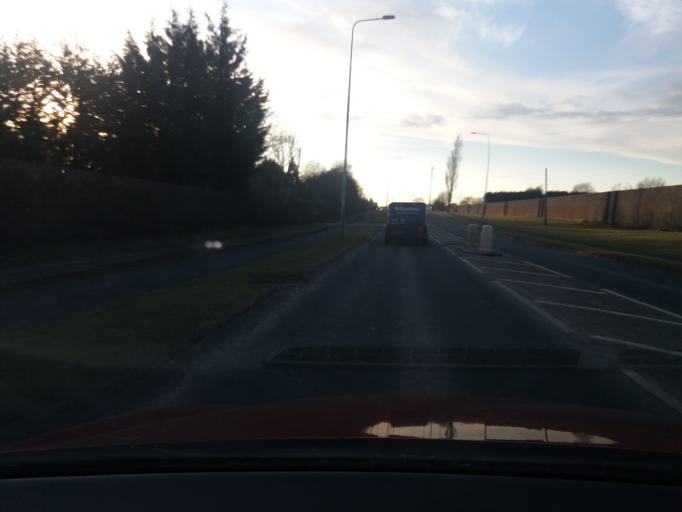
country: GB
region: England
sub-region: Lancashire
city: Euxton
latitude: 53.6698
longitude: -2.6509
